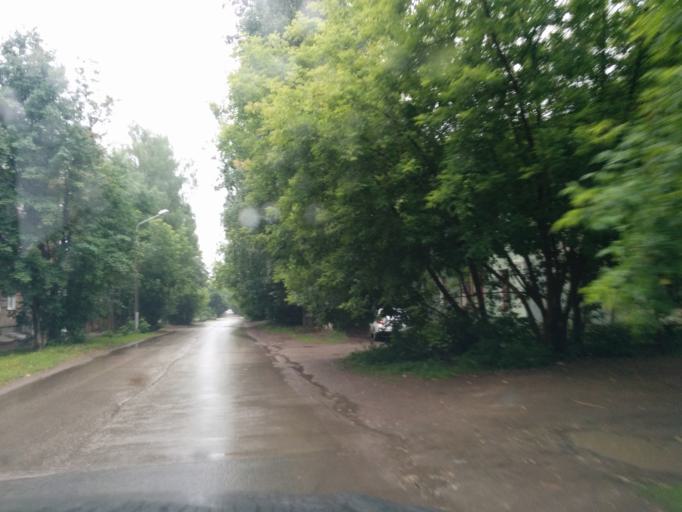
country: RU
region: Perm
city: Kondratovo
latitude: 58.0361
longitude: 56.0344
